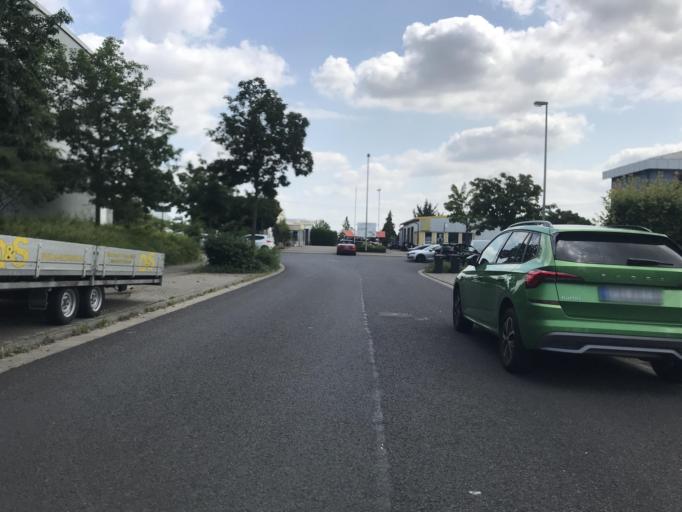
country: DE
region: Hesse
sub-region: Regierungsbezirk Darmstadt
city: Hochheim am Main
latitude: 50.0139
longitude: 8.3729
